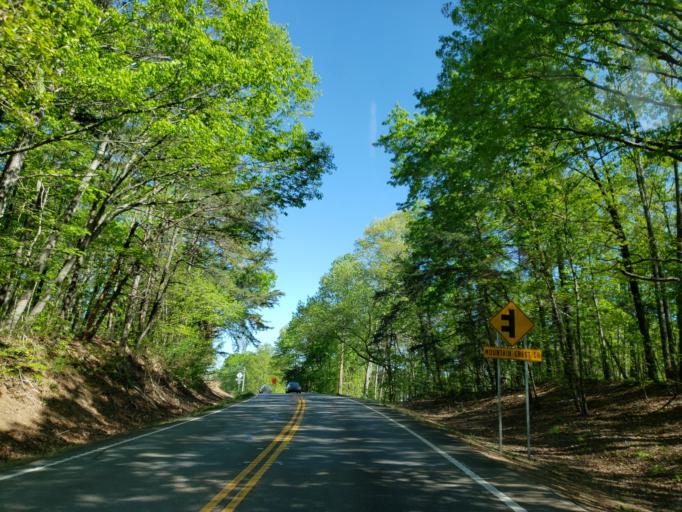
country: US
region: Georgia
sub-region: Cherokee County
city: Canton
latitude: 34.2868
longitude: -84.5194
